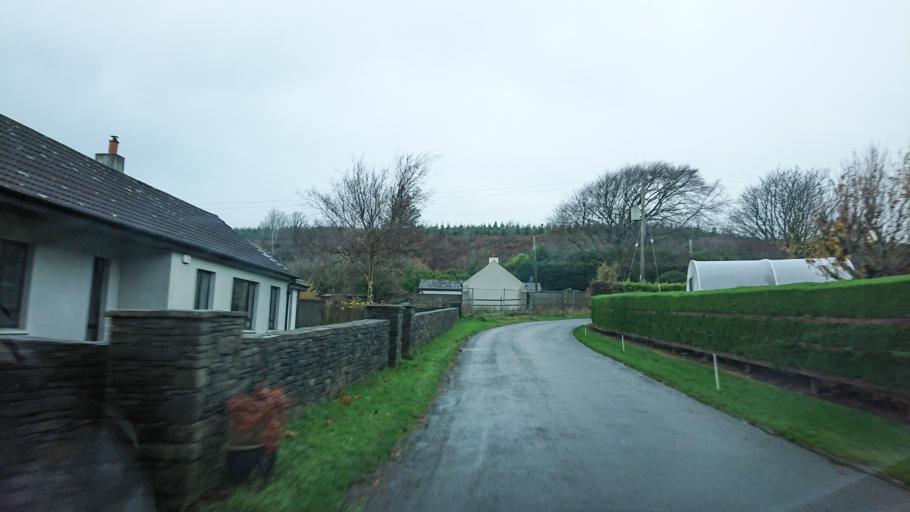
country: IE
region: Munster
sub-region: Waterford
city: Tra Mhor
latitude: 52.1953
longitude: -7.1316
